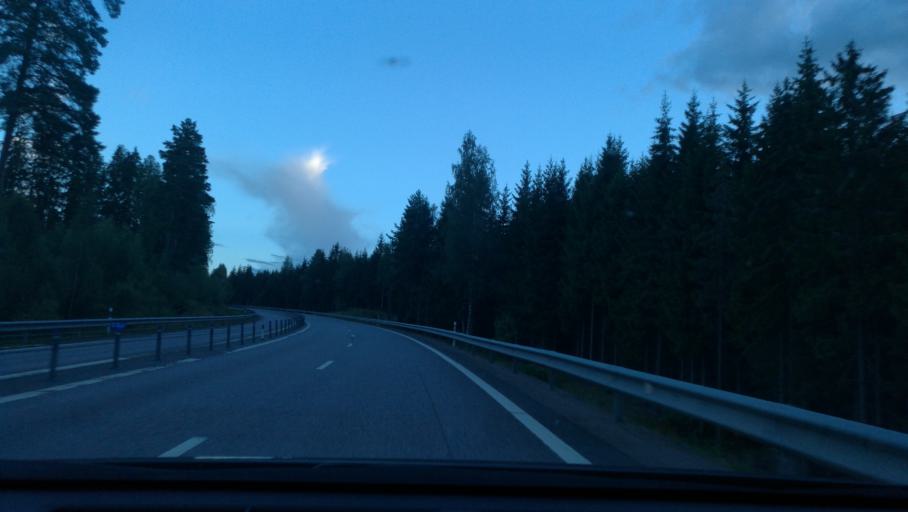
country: SE
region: Soedermanland
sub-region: Katrineholms Kommun
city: Katrineholm
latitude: 58.8419
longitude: 16.1971
